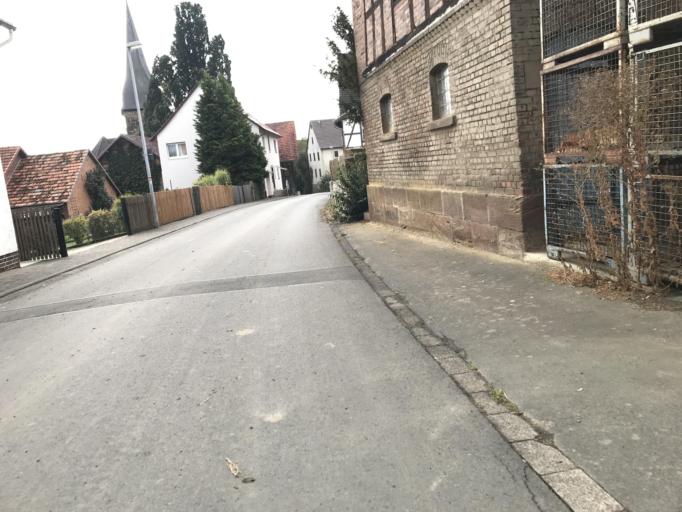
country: DE
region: Hesse
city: Gudensberg
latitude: 51.1949
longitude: 9.4041
